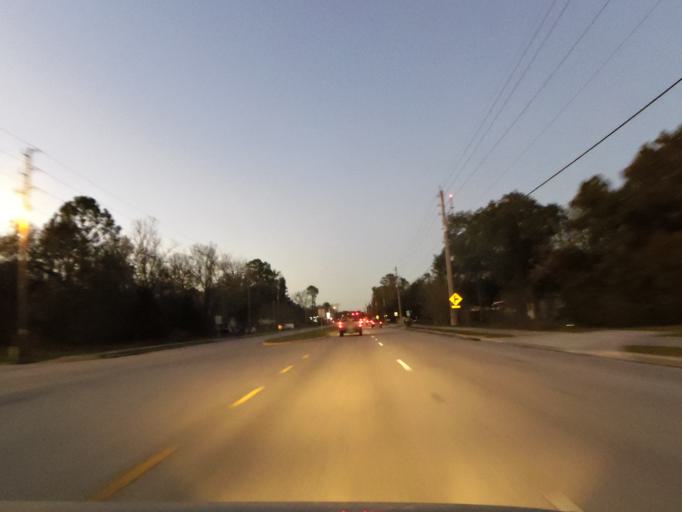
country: US
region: Florida
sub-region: Clay County
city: Lakeside
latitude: 30.1115
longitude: -81.7765
